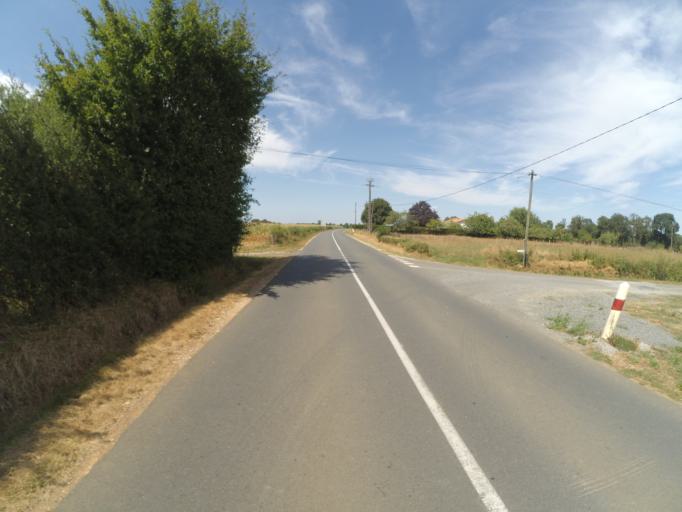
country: FR
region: Poitou-Charentes
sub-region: Departement de la Vienne
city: Availles-Limouzine
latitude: 46.1211
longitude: 0.5617
